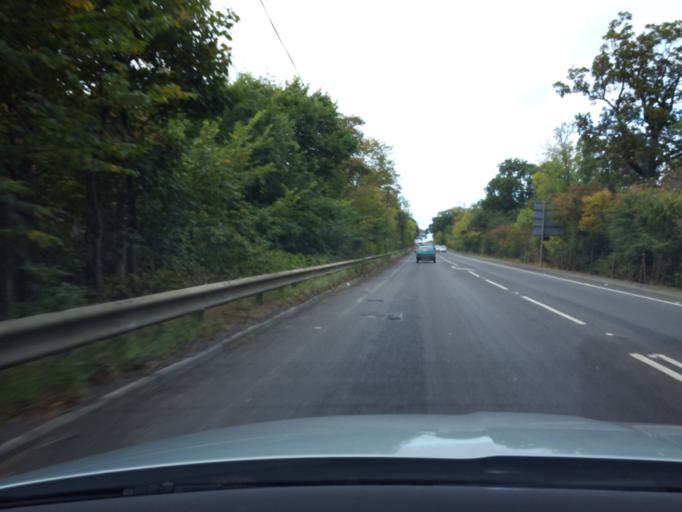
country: GB
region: Scotland
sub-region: Fife
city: Pathhead
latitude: 55.8850
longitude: -2.9918
